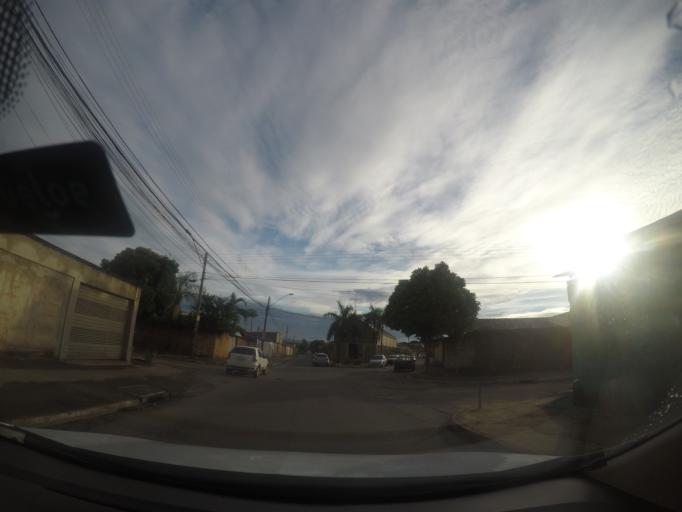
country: BR
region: Goias
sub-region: Goiania
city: Goiania
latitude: -16.6446
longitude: -49.3219
